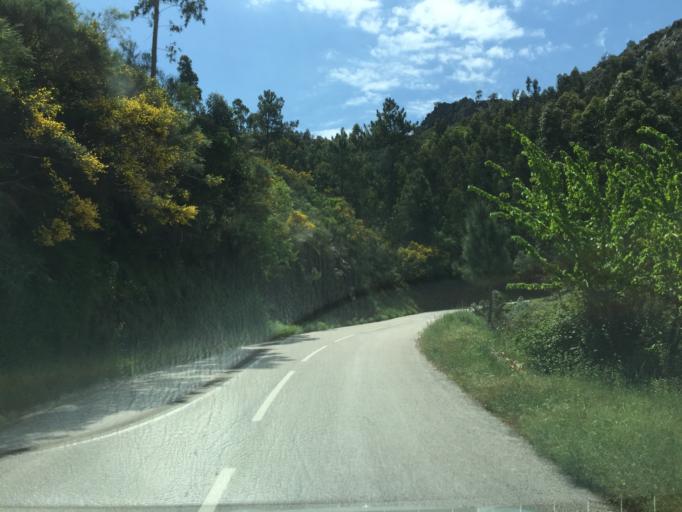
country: PT
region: Coimbra
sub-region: Pampilhosa da Serra
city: Pampilhosa da Serra
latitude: 40.0864
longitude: -7.8607
